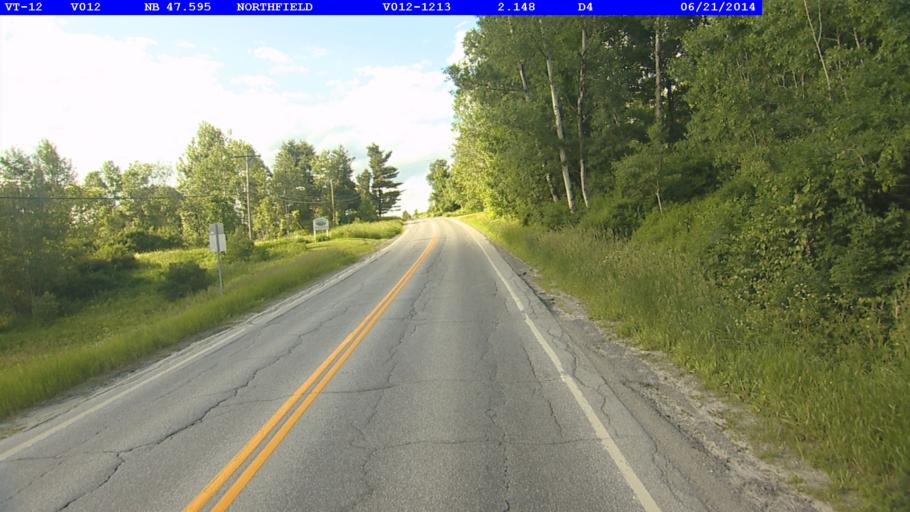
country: US
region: Vermont
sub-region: Washington County
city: Northfield
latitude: 44.1201
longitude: -72.6561
